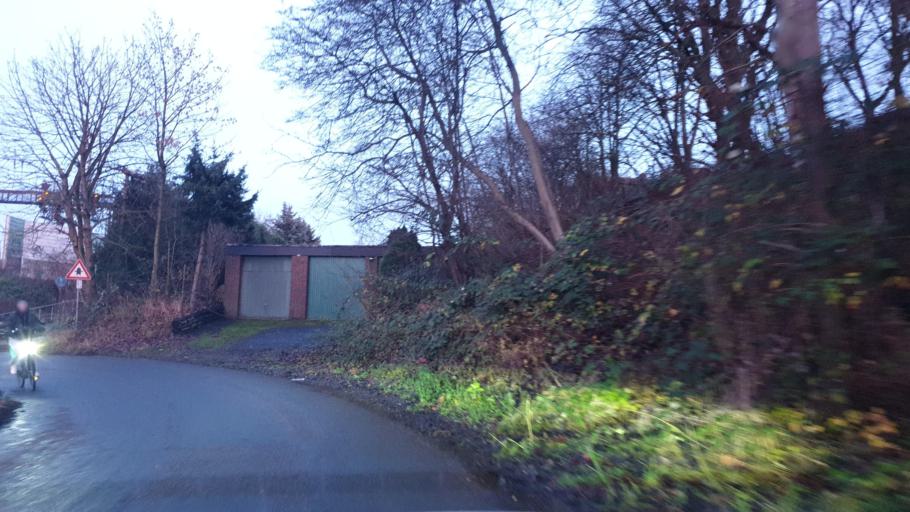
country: DE
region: Lower Saxony
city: Osnabrueck
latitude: 52.2615
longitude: 8.0394
